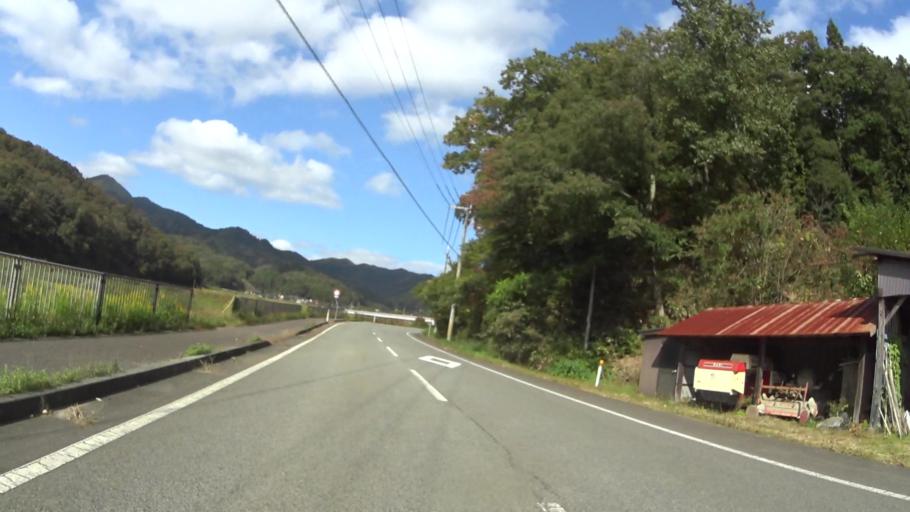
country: JP
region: Hyogo
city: Toyooka
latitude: 35.5008
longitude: 134.9925
